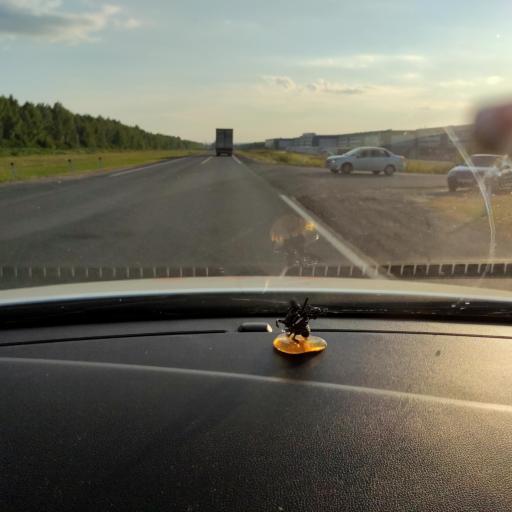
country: RU
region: Tatarstan
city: Stolbishchi
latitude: 55.6336
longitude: 49.2634
